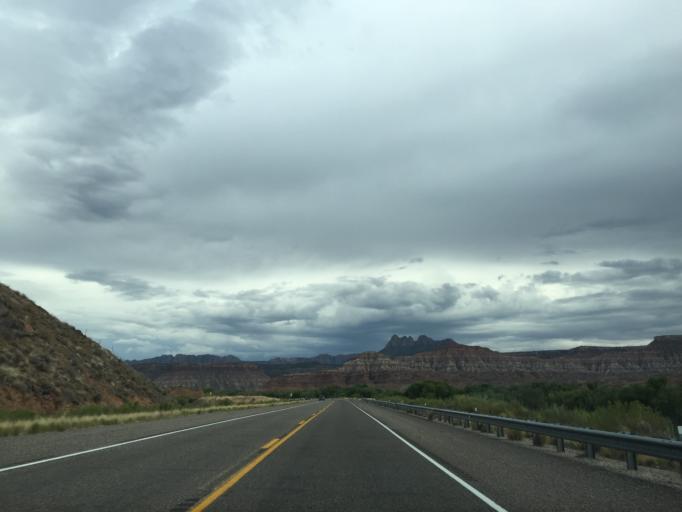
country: US
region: Utah
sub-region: Washington County
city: LaVerkin
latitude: 37.1857
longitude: -113.1372
